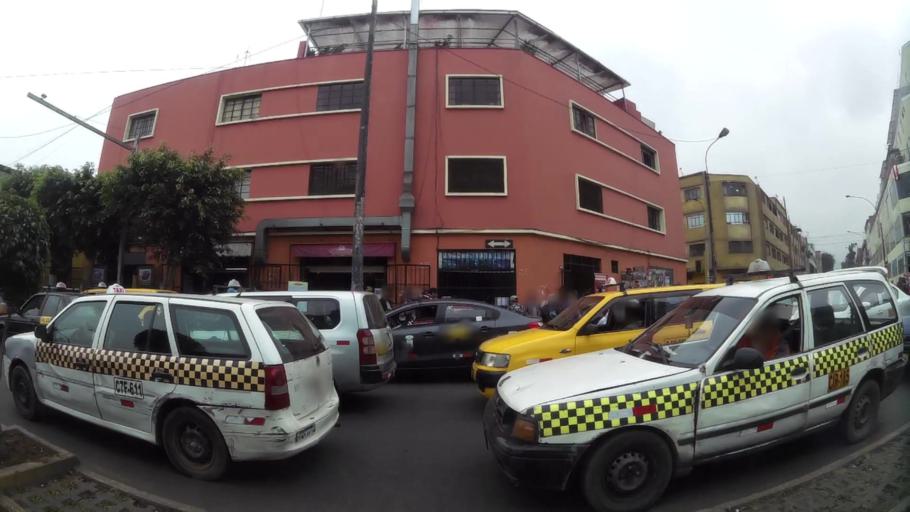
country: PE
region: Lima
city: Lima
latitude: -12.0573
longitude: -77.0259
